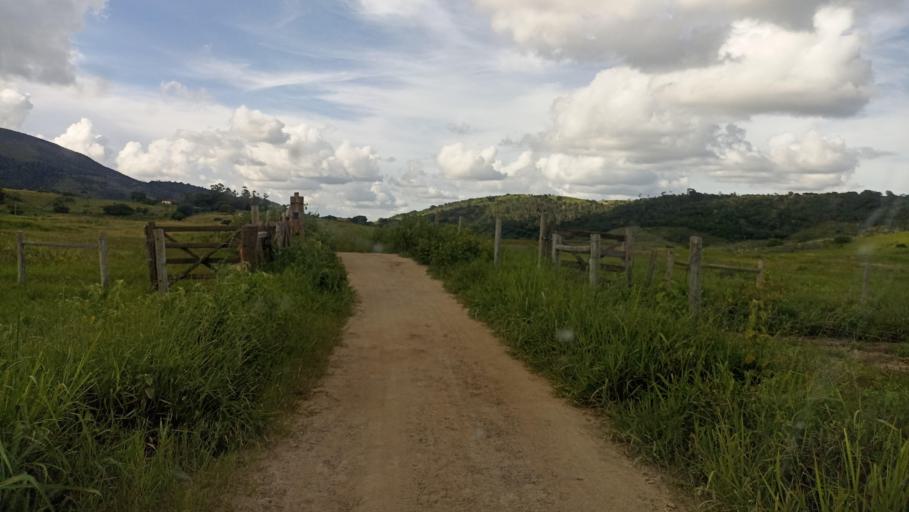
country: BR
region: Minas Gerais
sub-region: Almenara
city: Almenara
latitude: -16.6187
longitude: -40.4648
